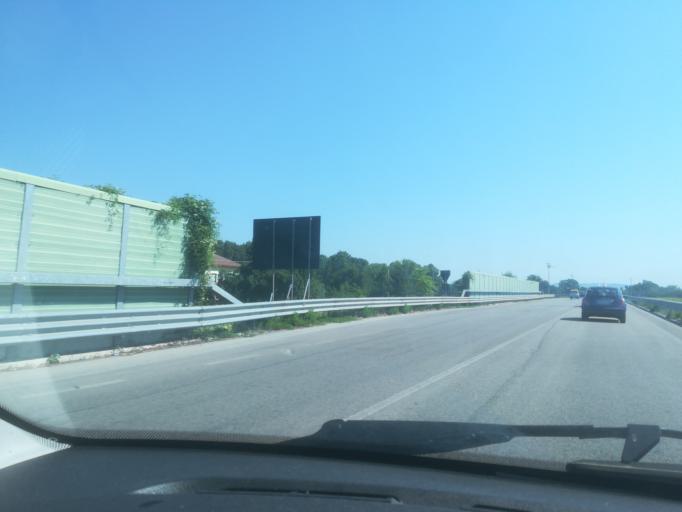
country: IT
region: The Marches
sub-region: Provincia di Macerata
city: Villa Potenza
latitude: 43.3270
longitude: 13.4288
